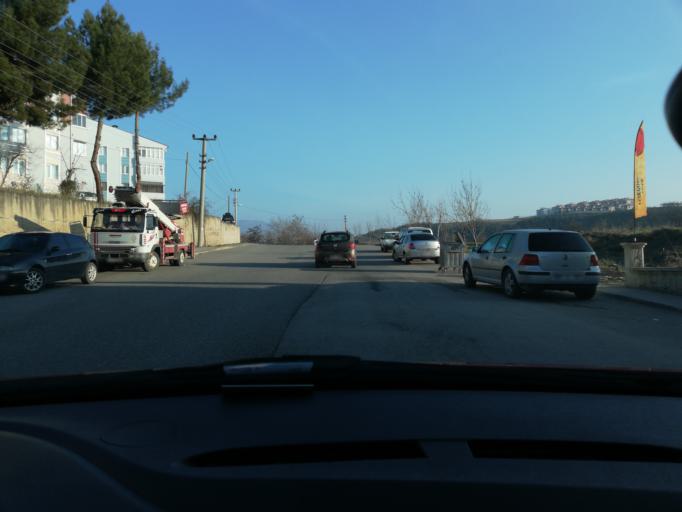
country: TR
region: Karabuk
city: Safranbolu
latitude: 41.2218
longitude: 32.6727
